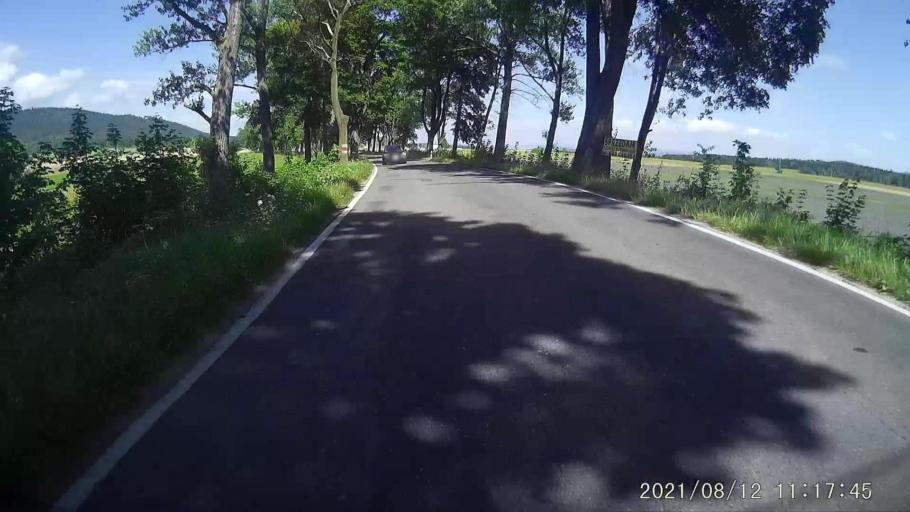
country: PL
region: Lower Silesian Voivodeship
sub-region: Powiat klodzki
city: Bystrzyca Klodzka
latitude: 50.3118
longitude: 16.6220
